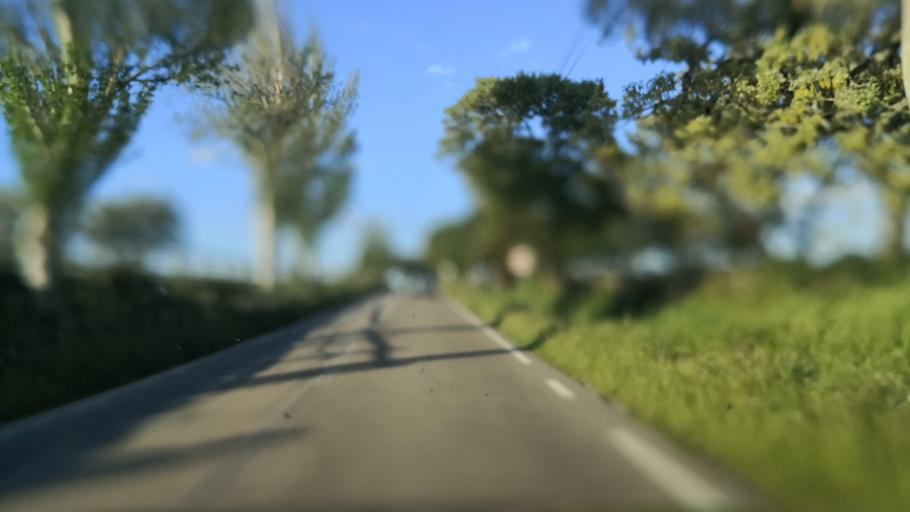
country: PT
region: Portalegre
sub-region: Portalegre
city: Reguengo
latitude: 39.3403
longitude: -7.4130
